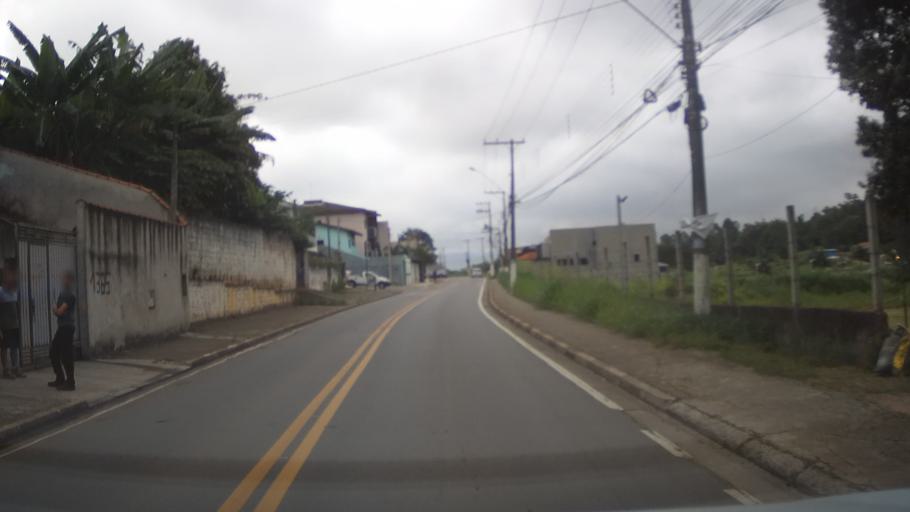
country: BR
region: Sao Paulo
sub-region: Aruja
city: Aruja
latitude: -23.4007
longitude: -46.3419
